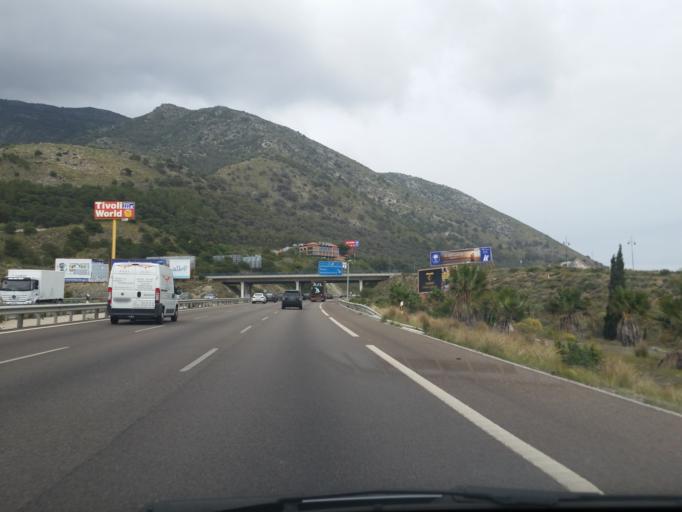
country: ES
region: Andalusia
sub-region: Provincia de Malaga
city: Mijas
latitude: 36.5834
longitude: -4.6044
